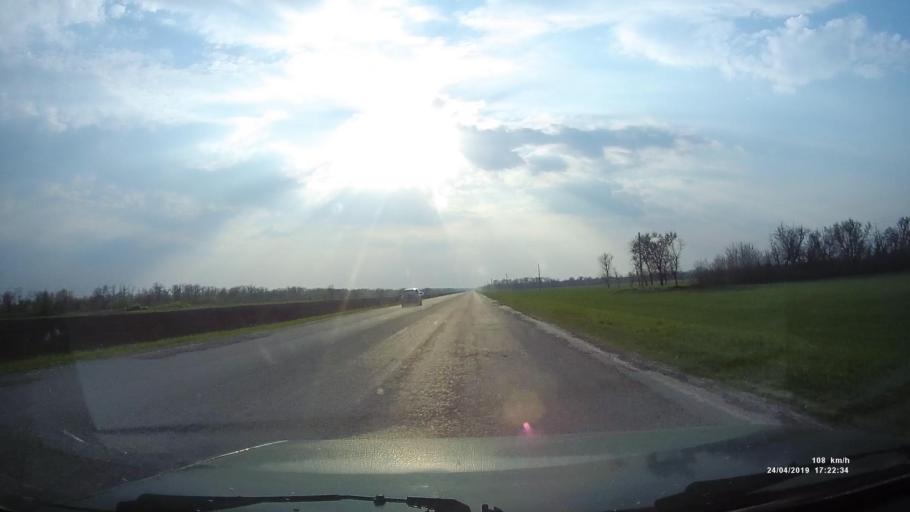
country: RU
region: Rostov
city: Gigant
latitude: 46.5210
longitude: 41.3058
